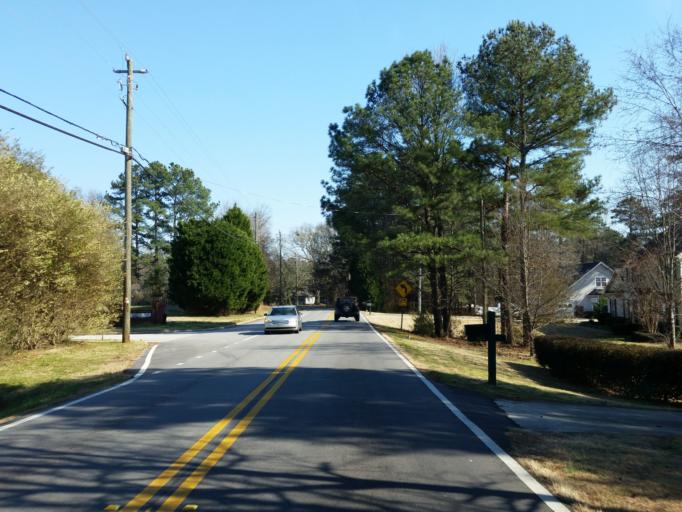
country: US
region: Georgia
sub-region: Henry County
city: Stockbridge
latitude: 33.4758
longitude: -84.2326
